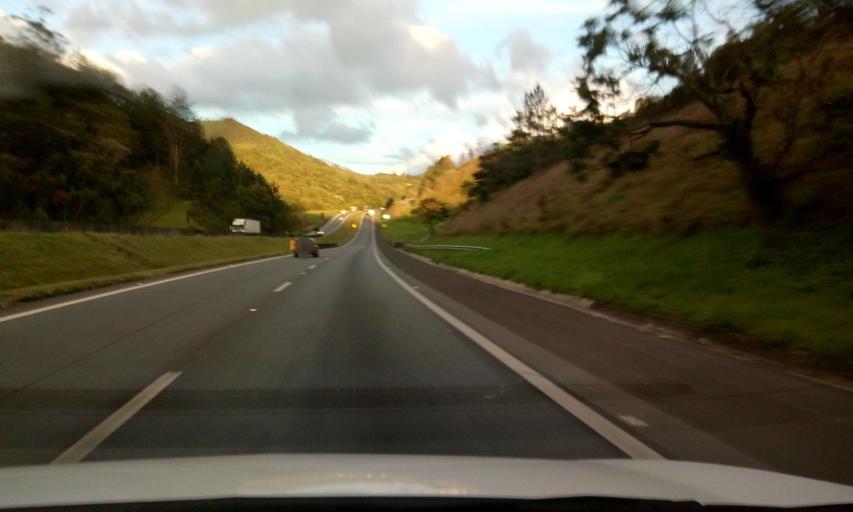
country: BR
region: Sao Paulo
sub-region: Piracaia
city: Piracaia
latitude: -23.1733
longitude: -46.2776
